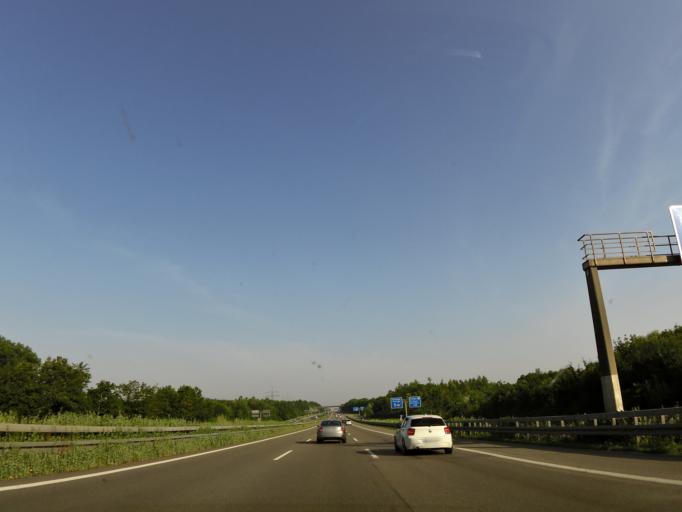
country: DE
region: Baden-Wuerttemberg
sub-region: Regierungsbezirk Stuttgart
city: Unterensingen
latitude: 48.6687
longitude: 9.3611
